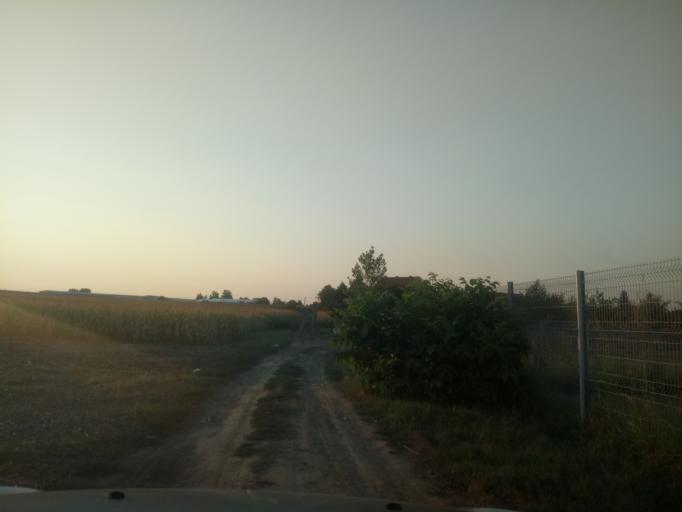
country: RS
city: Stari Banovci
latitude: 44.9816
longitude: 20.2677
